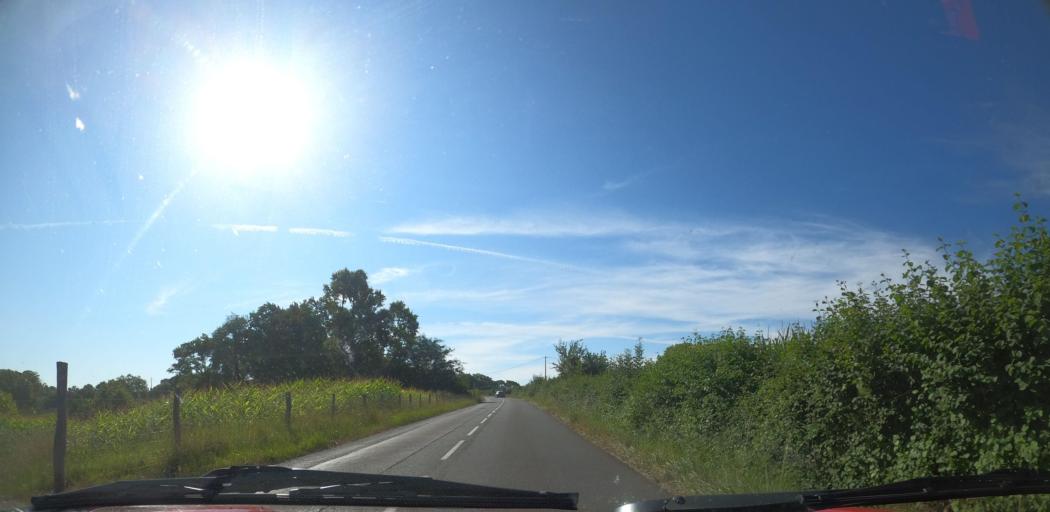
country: FR
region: Aquitaine
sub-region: Departement des Pyrenees-Atlantiques
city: Arbonne
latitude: 43.4076
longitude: -1.5441
